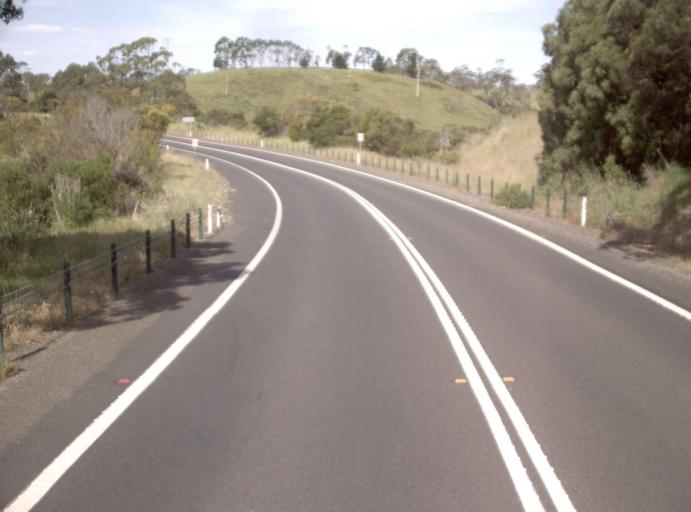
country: AU
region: Victoria
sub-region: East Gippsland
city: Lakes Entrance
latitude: -37.8535
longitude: 148.0349
